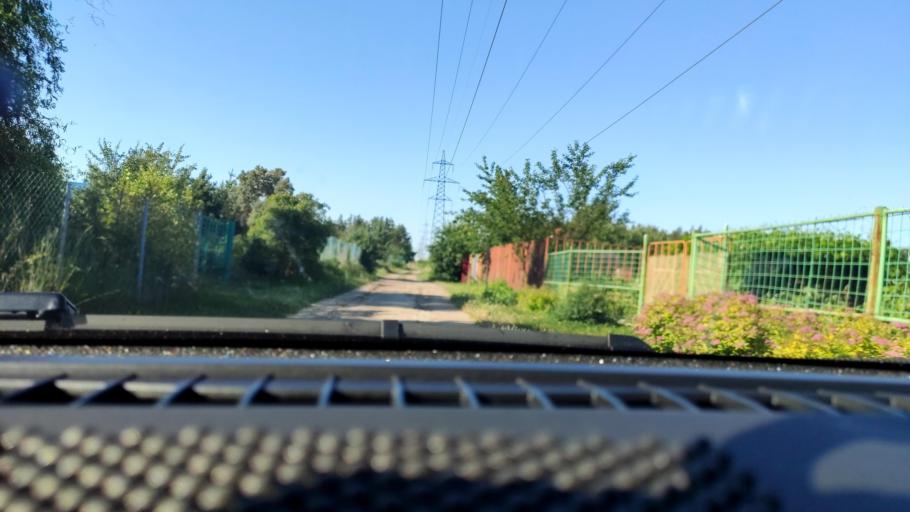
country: RU
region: Voronezj
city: Volya
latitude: 51.7418
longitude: 39.4601
